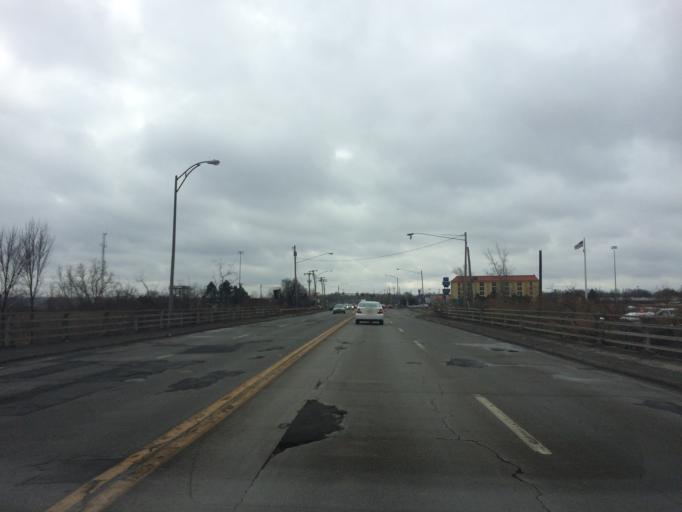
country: US
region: New York
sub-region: Monroe County
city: Rochester
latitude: 43.1106
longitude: -77.6160
